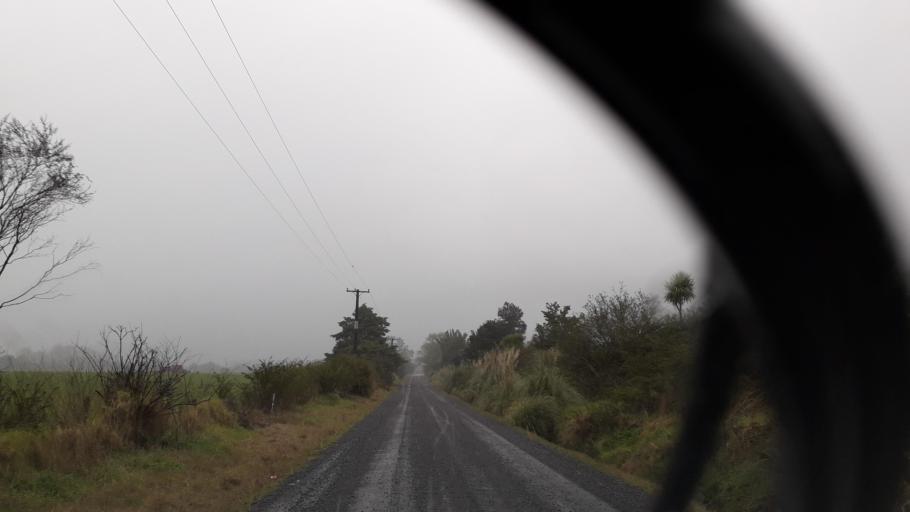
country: NZ
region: Northland
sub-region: Far North District
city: Waimate North
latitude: -35.4947
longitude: 173.6996
